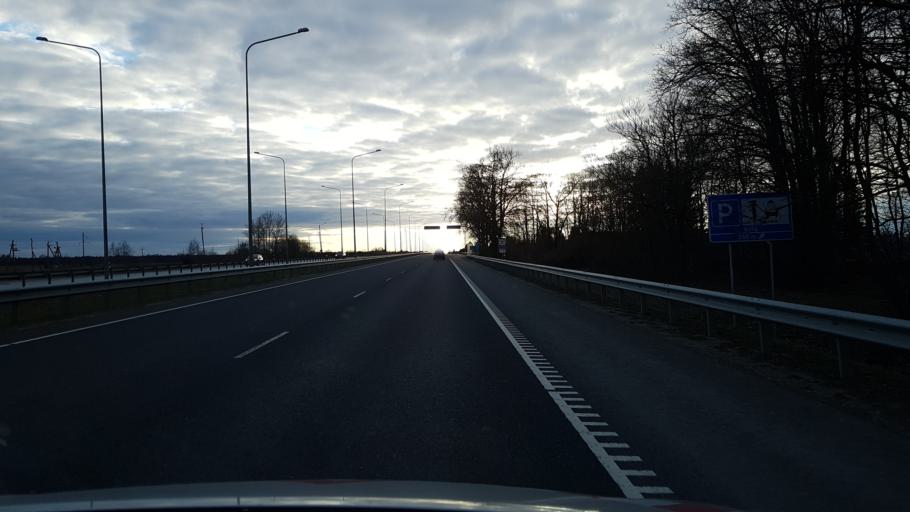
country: EE
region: Harju
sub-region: Kuusalu vald
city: Kuusalu
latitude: 59.4460
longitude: 25.3858
